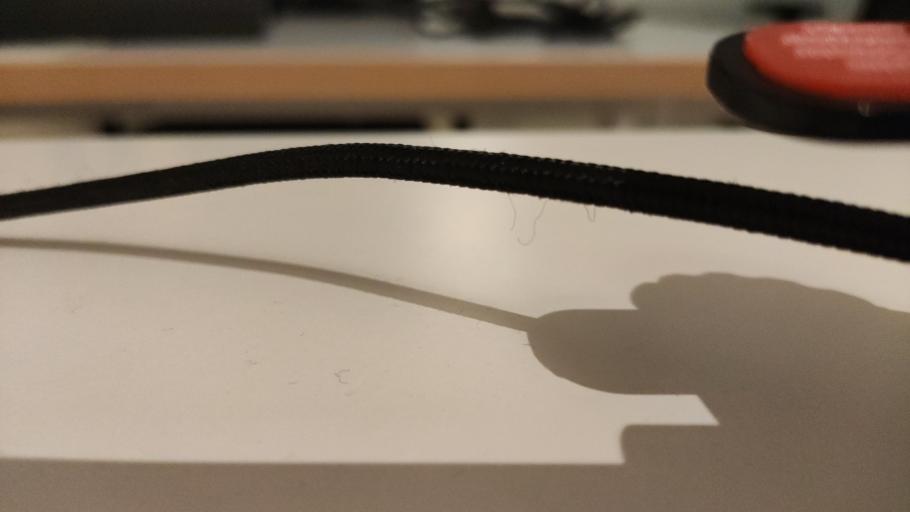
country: RU
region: Moskovskaya
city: Novoye
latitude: 55.6576
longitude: 38.9378
